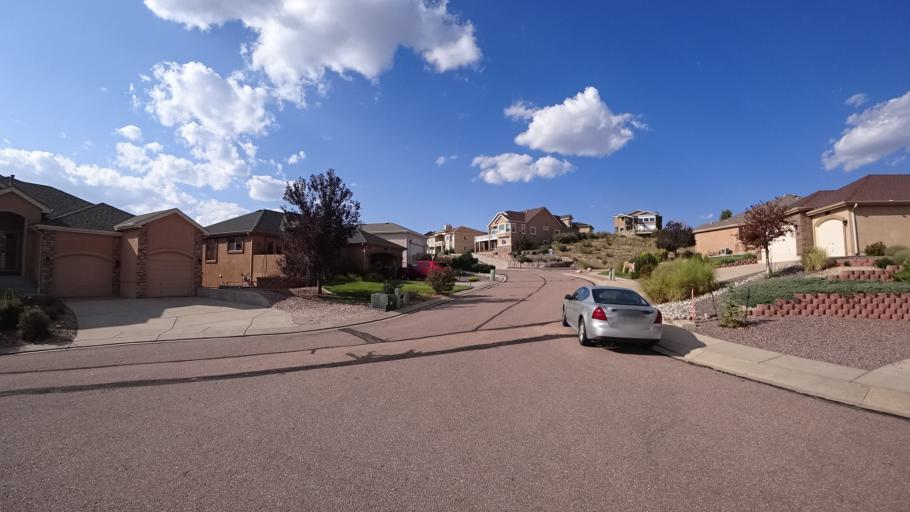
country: US
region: Colorado
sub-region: El Paso County
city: Cimarron Hills
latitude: 38.9115
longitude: -104.7364
